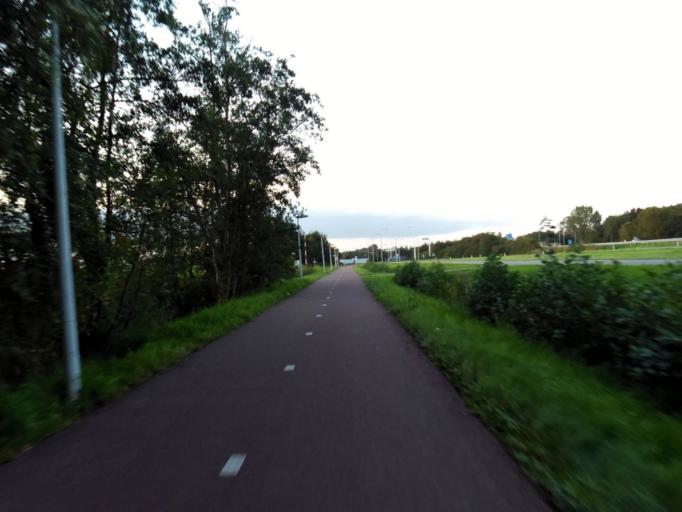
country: NL
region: South Holland
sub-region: Gemeente Voorschoten
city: Voorschoten
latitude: 52.1564
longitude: 4.4431
